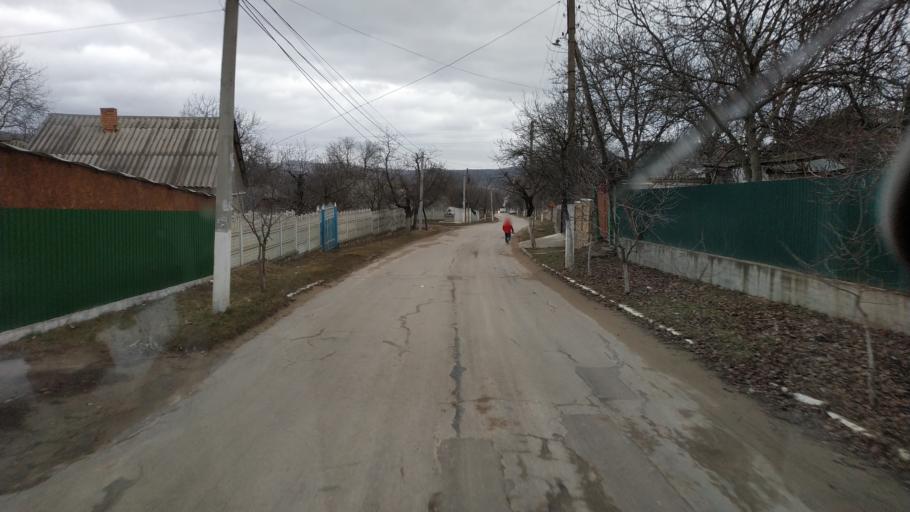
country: MD
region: Calarasi
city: Calarasi
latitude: 47.2613
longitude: 28.1354
